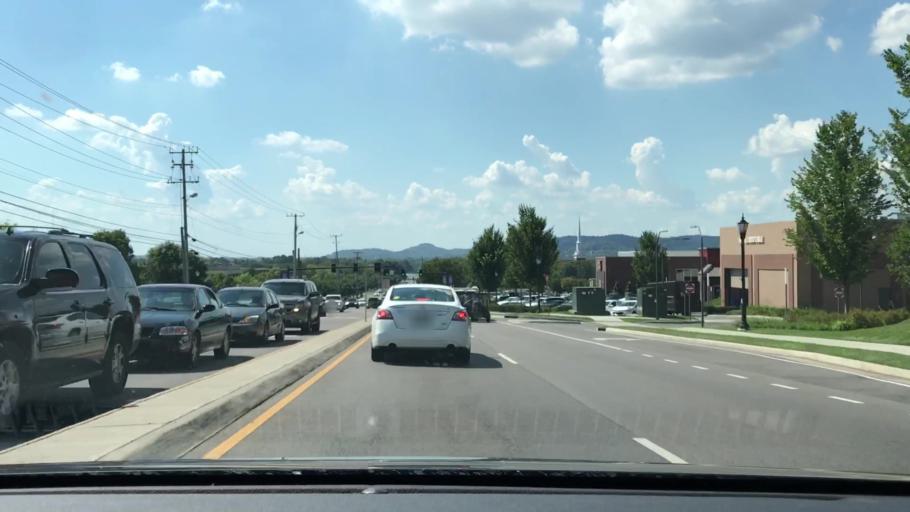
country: US
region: Tennessee
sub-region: Williamson County
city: Brentwood
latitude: 36.0331
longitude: -86.7889
